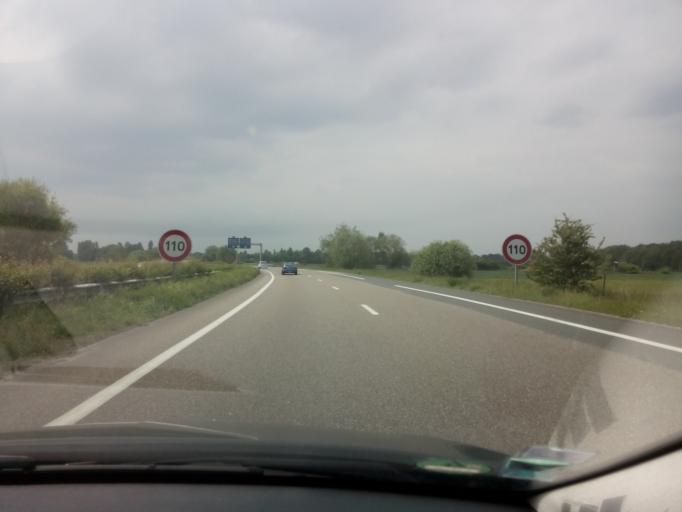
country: FR
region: Alsace
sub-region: Departement du Bas-Rhin
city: Reichstett
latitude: 48.6739
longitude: 7.7438
